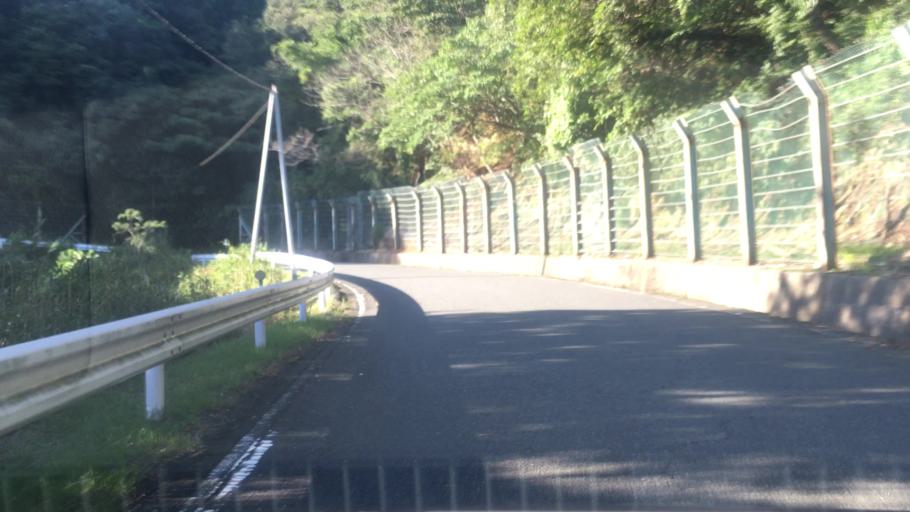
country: JP
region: Hyogo
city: Toyooka
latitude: 35.6151
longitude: 134.8765
